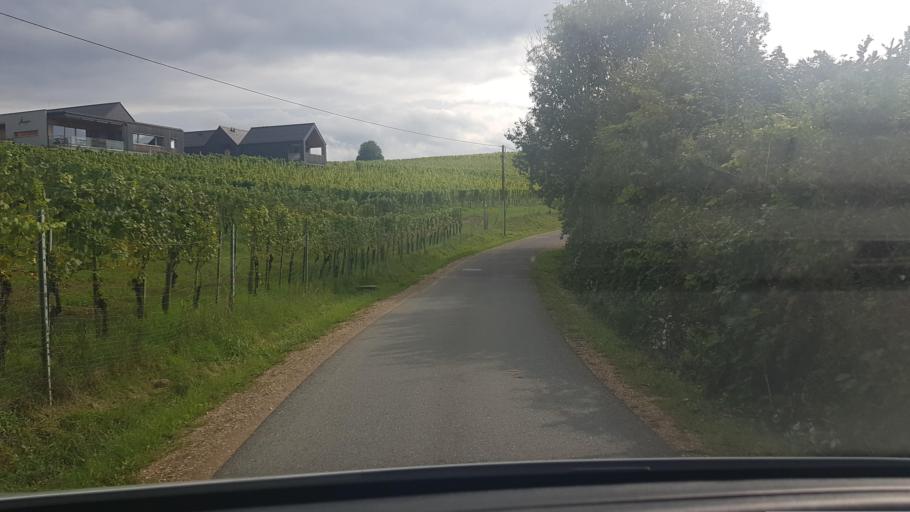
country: AT
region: Styria
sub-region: Politischer Bezirk Leibnitz
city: Grossklein
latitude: 46.7121
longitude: 15.4329
